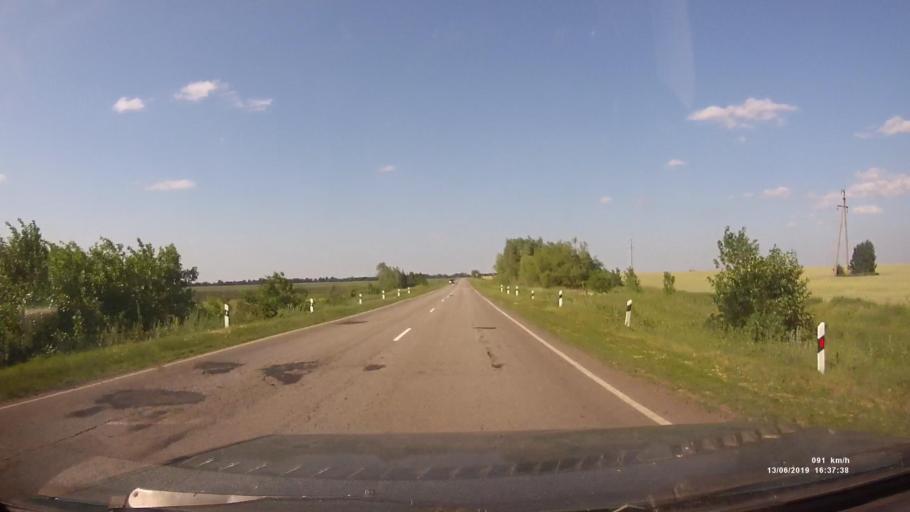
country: RU
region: Rostov
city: Kazanskaya
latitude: 49.9094
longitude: 41.3152
